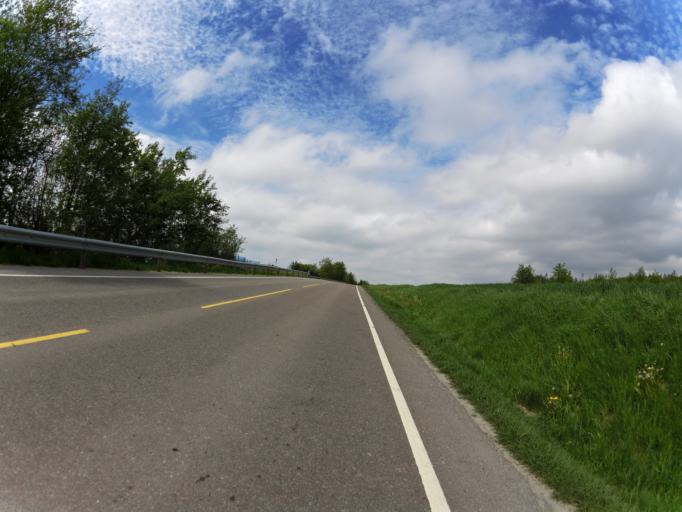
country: NO
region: Ostfold
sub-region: Rade
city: Karlshus
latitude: 59.3270
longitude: 10.9407
